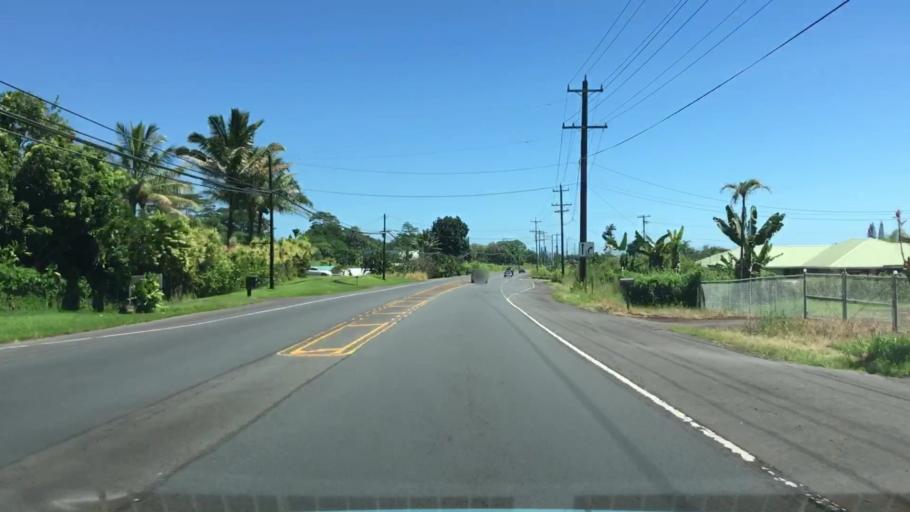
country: US
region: Hawaii
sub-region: Hawaii County
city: Kurtistown
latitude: 19.6024
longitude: -155.0528
